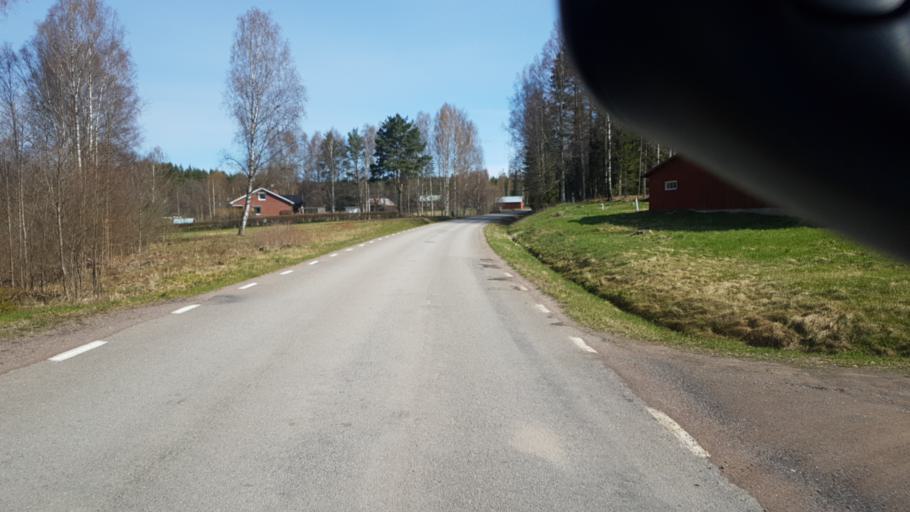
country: SE
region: Vaermland
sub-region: Arvika Kommun
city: Arvika
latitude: 59.5520
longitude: 12.7408
